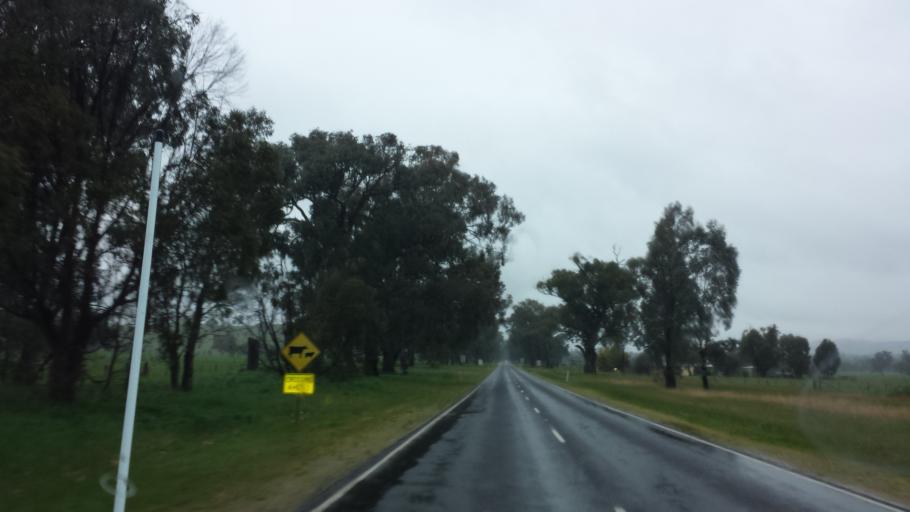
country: AU
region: Victoria
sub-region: Wangaratta
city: Wangaratta
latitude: -36.4374
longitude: 146.5452
